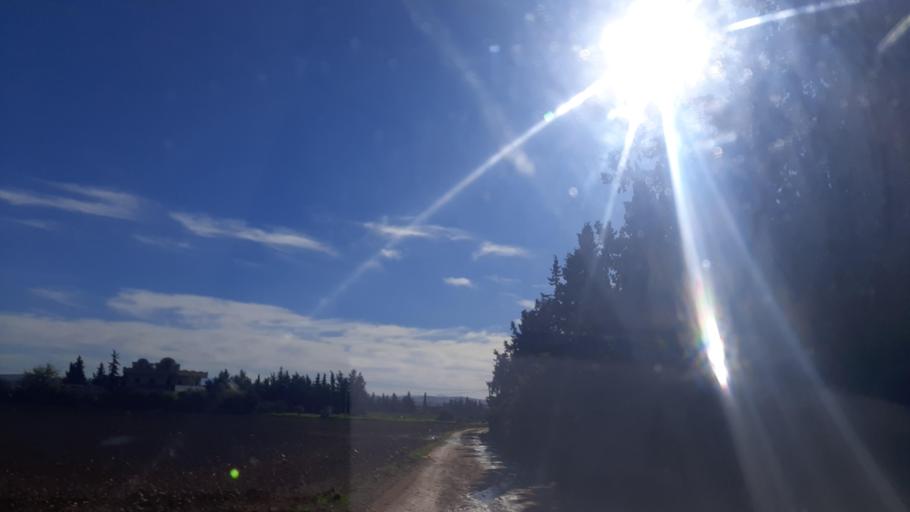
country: TN
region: Tunis
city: Oued Lill
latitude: 36.7596
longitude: 9.9819
